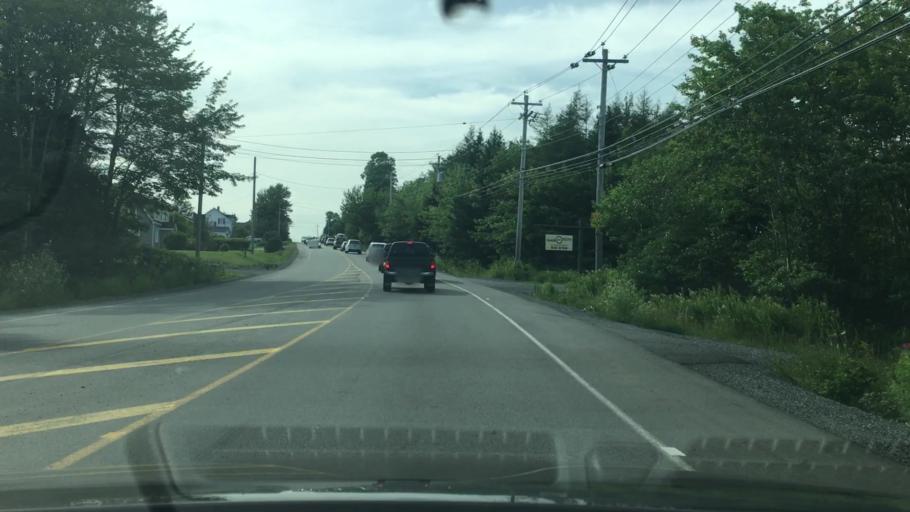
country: CA
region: Nova Scotia
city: Dartmouth
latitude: 44.7294
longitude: -63.7507
